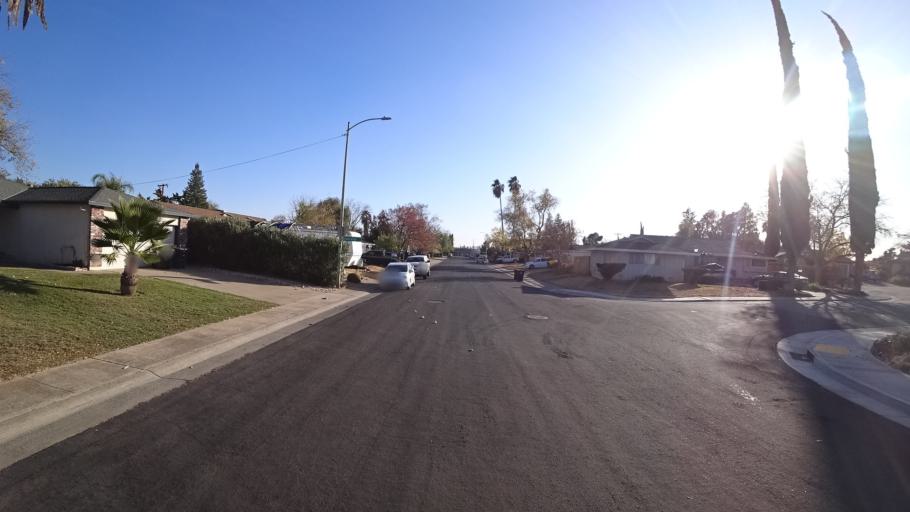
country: US
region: California
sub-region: Sacramento County
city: Citrus Heights
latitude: 38.6992
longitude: -121.2926
